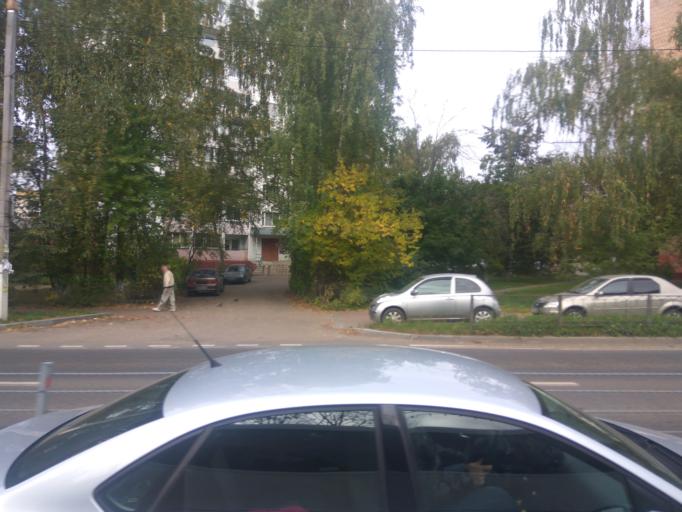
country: RU
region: Moskovskaya
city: Fryazino
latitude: 55.9525
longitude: 38.0524
